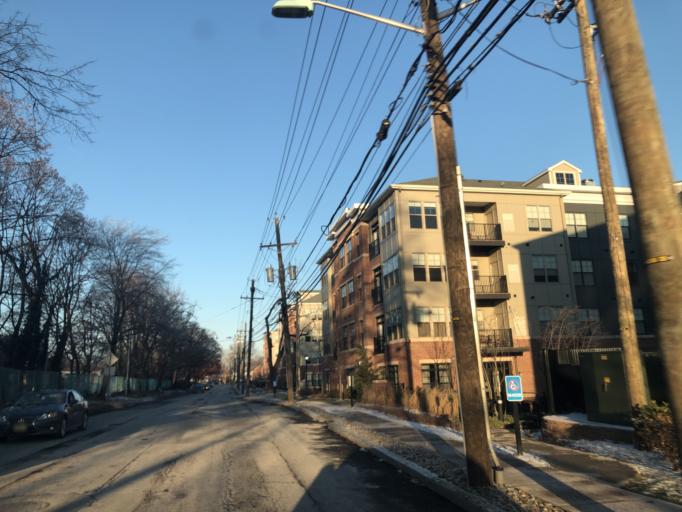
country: US
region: New Jersey
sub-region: Essex County
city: Irvington
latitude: 40.7234
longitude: -74.2536
